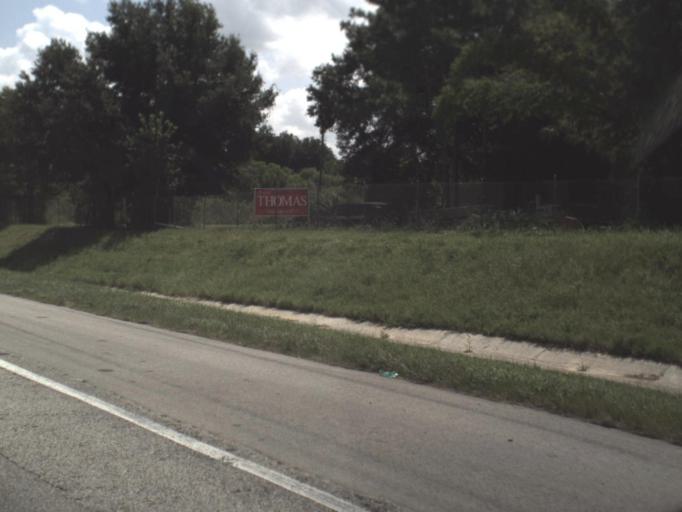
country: US
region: Florida
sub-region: Hillsborough County
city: Seffner
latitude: 28.0115
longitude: -82.2790
